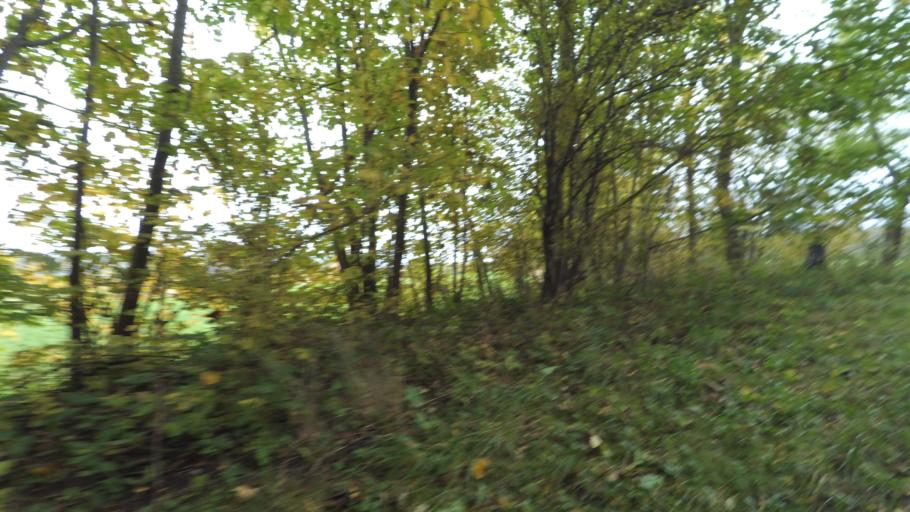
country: DK
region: Central Jutland
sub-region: Arhus Kommune
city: Stavtrup
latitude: 56.1483
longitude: 10.1032
